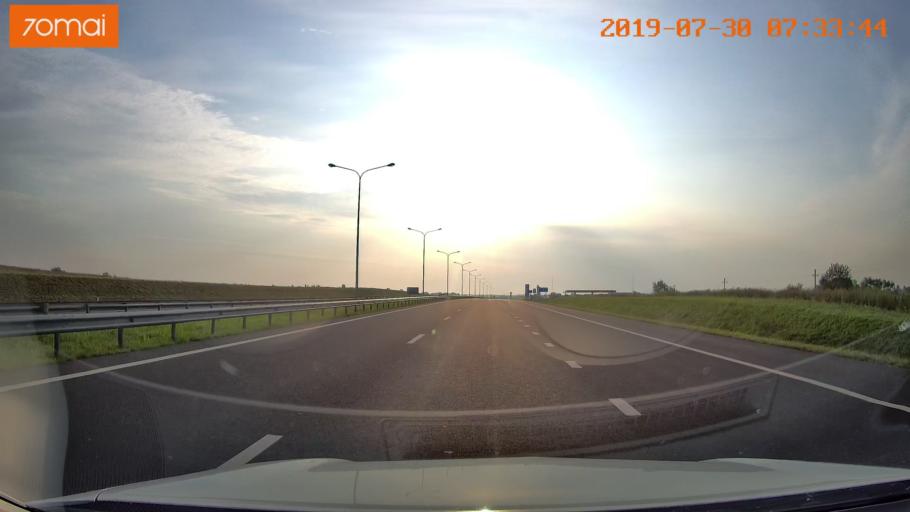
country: RU
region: Kaliningrad
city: Gvardeysk
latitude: 54.6707
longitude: 21.0527
